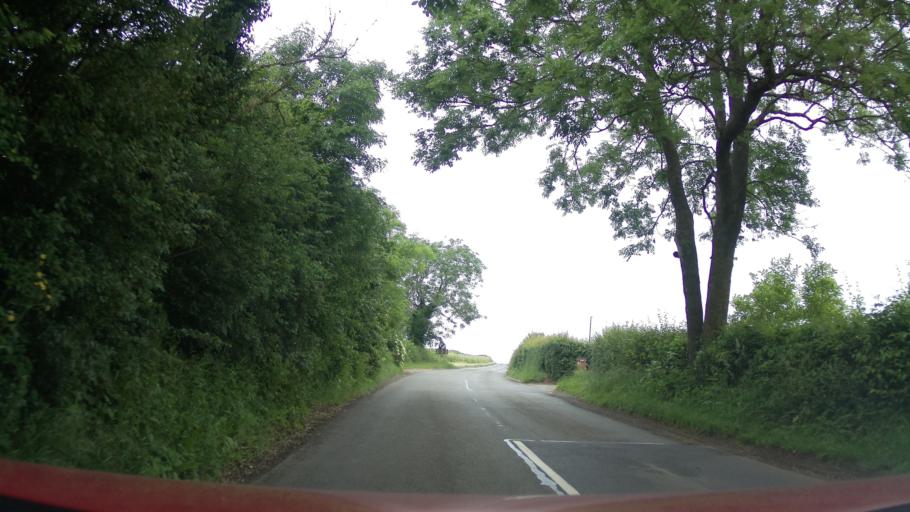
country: GB
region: England
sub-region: Leicestershire
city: Melton Mowbray
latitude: 52.6958
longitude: -0.8404
